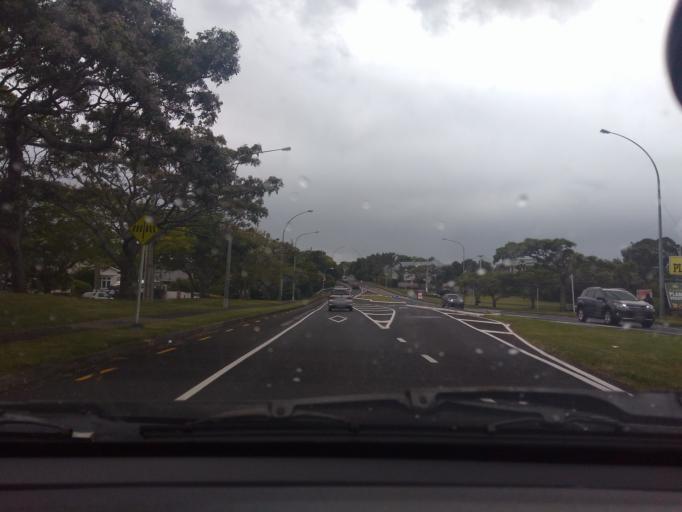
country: NZ
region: Auckland
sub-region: Auckland
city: Auckland
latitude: -36.8743
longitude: 174.7257
